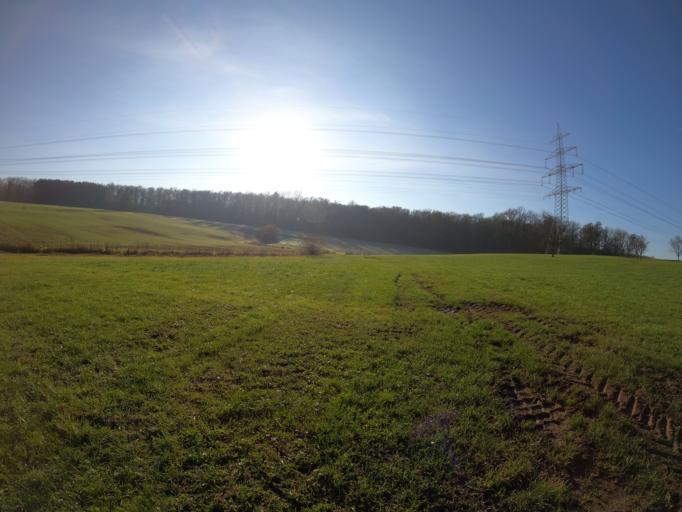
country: DE
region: Baden-Wuerttemberg
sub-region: Regierungsbezirk Stuttgart
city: Albershausen
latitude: 48.7041
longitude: 9.5525
